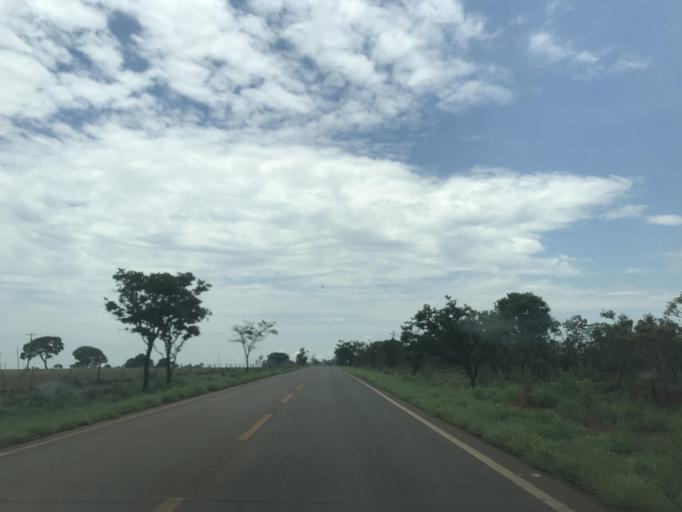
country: BR
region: Goias
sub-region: Luziania
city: Luziania
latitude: -16.2888
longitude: -48.0037
